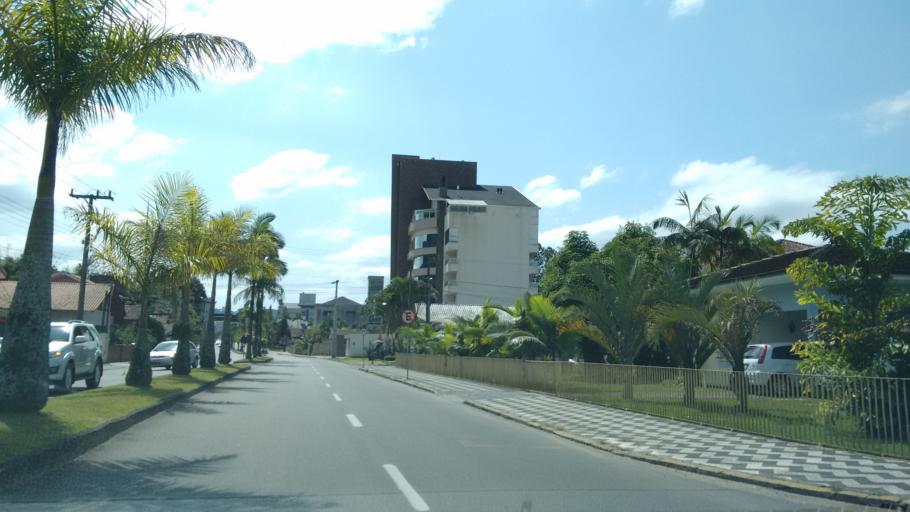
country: BR
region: Santa Catarina
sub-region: Pomerode
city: Pomerode
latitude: -26.7360
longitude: -49.1785
